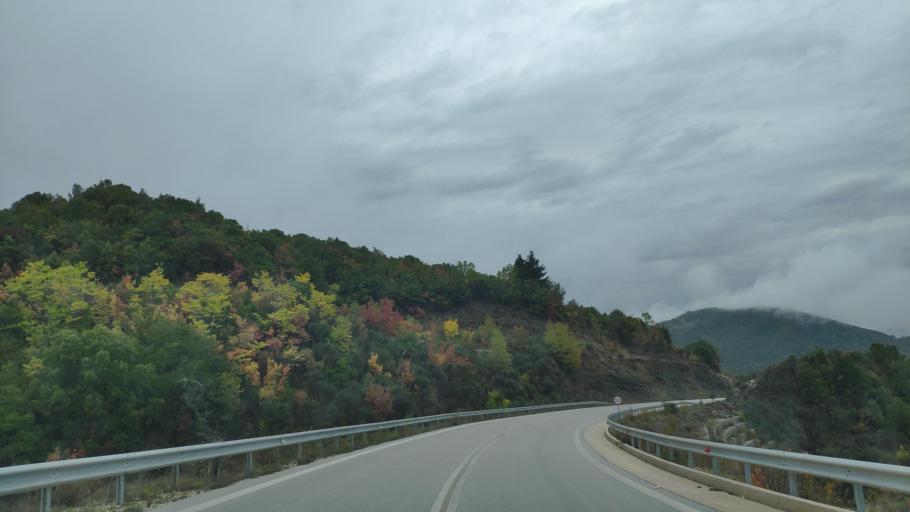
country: GR
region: Epirus
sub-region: Nomos Thesprotias
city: Paramythia
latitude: 39.4815
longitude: 20.6738
